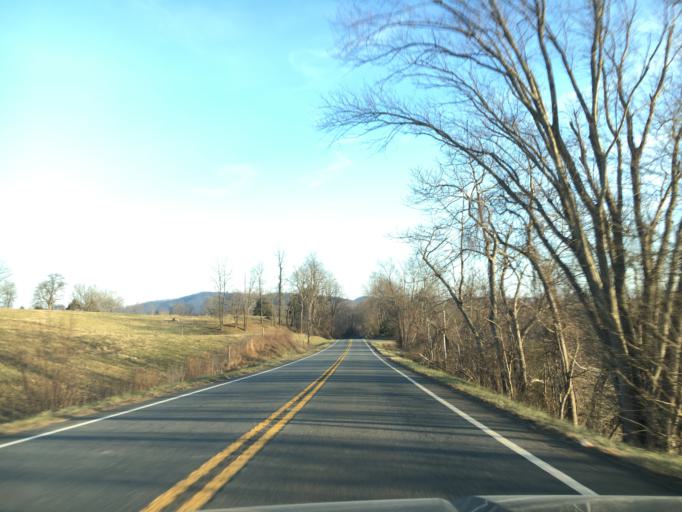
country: US
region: Virginia
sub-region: Rappahannock County
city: Washington
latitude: 38.6485
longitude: -78.2121
